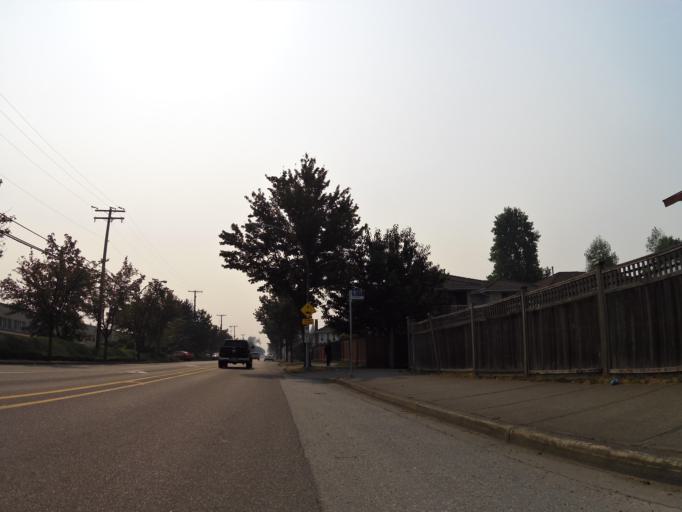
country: CA
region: British Columbia
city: Delta
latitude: 49.1518
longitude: -122.8791
